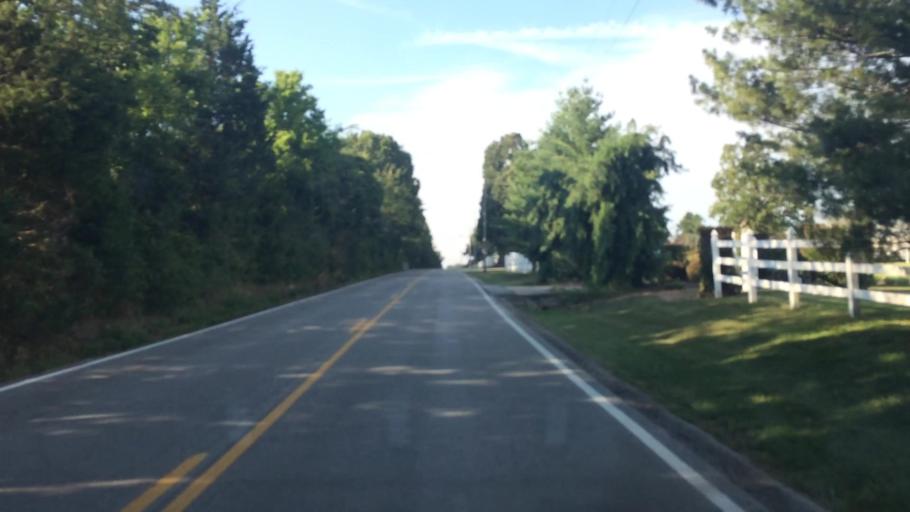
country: US
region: Missouri
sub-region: Greene County
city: Strafford
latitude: 37.2655
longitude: -93.1877
